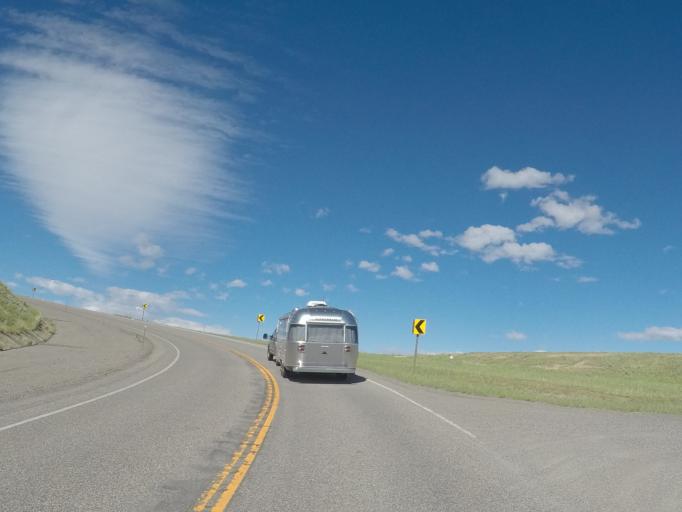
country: US
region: Montana
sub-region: Carbon County
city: Red Lodge
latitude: 45.1719
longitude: -109.2107
